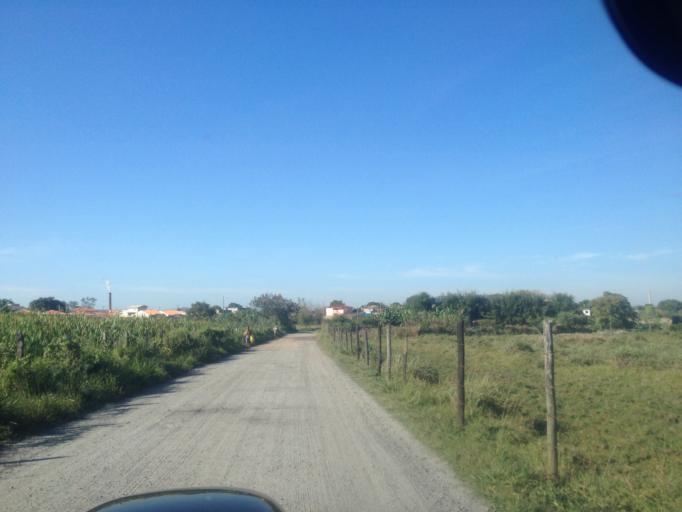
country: BR
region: Rio de Janeiro
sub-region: Porto Real
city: Porto Real
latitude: -22.4046
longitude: -44.2974
